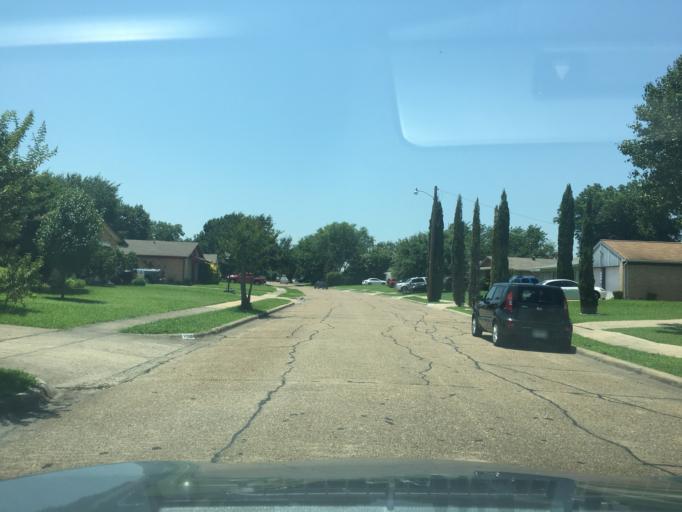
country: US
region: Texas
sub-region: Dallas County
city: Richardson
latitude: 32.9290
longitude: -96.6951
